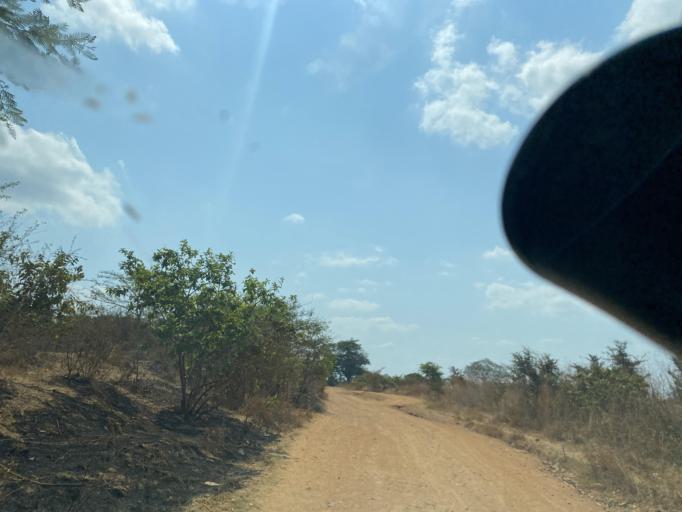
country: ZM
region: Lusaka
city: Chongwe
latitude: -15.6029
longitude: 28.7400
